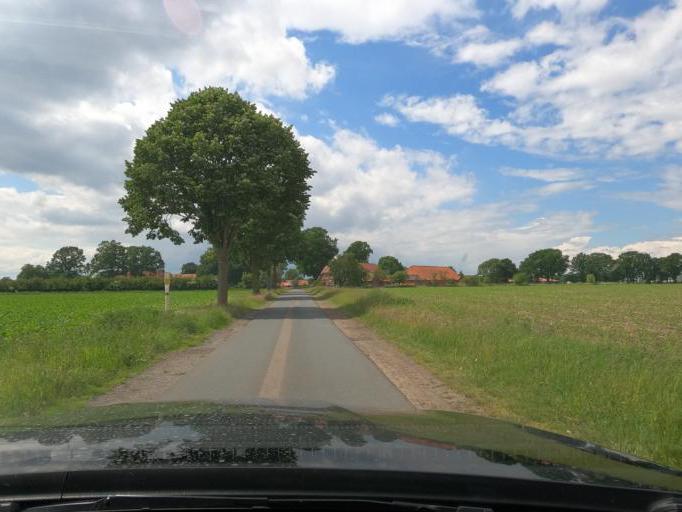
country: DE
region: Lower Saxony
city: Steimbke
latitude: 52.6311
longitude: 9.3964
